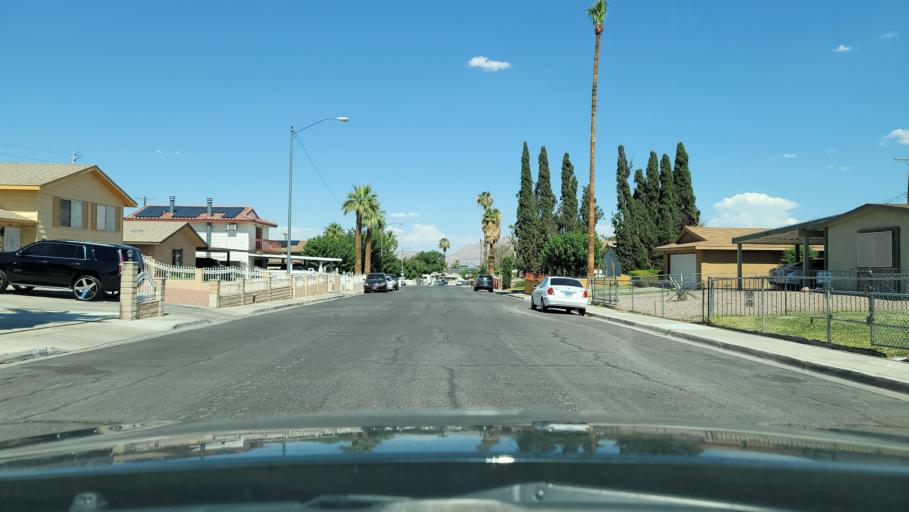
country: US
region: Nevada
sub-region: Clark County
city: Las Vegas
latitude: 36.2013
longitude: -115.1491
